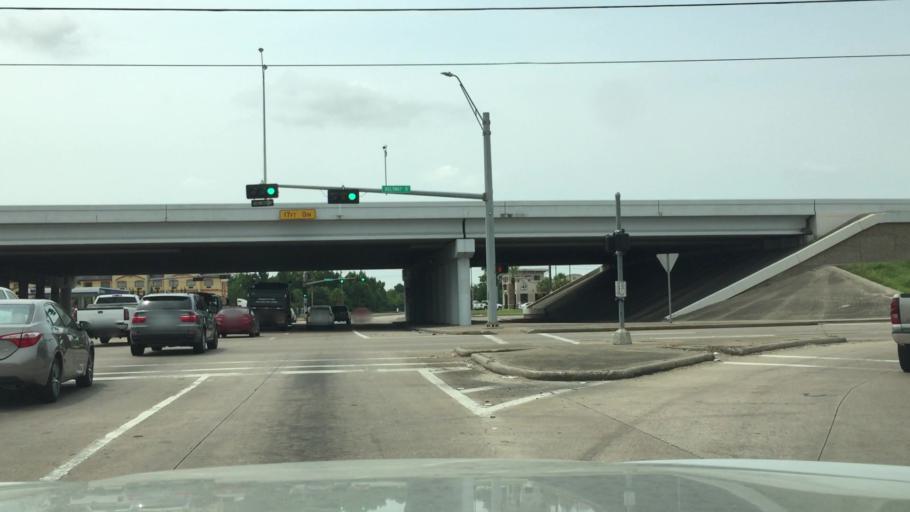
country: US
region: Texas
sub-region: Harris County
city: Jersey Village
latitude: 29.9305
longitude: -95.5446
